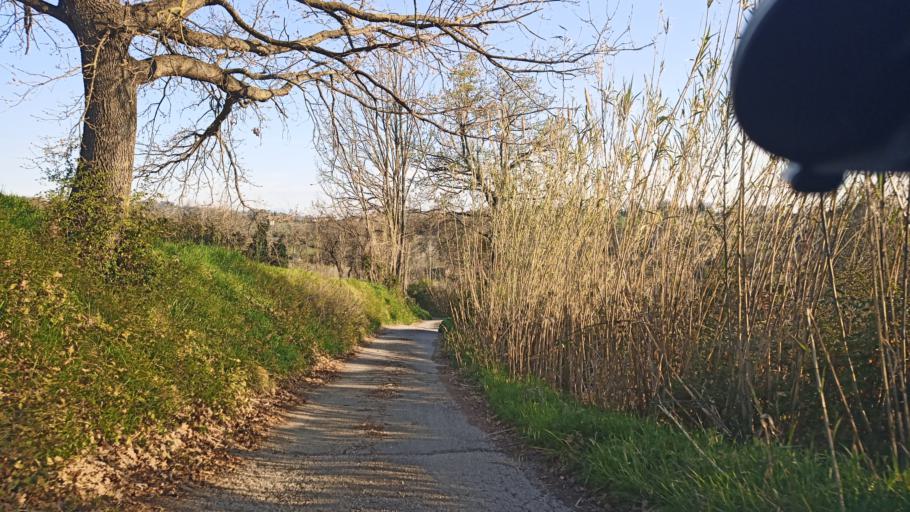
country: IT
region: Latium
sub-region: Provincia di Rieti
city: Poggio Mirteto
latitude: 42.2648
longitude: 12.6619
